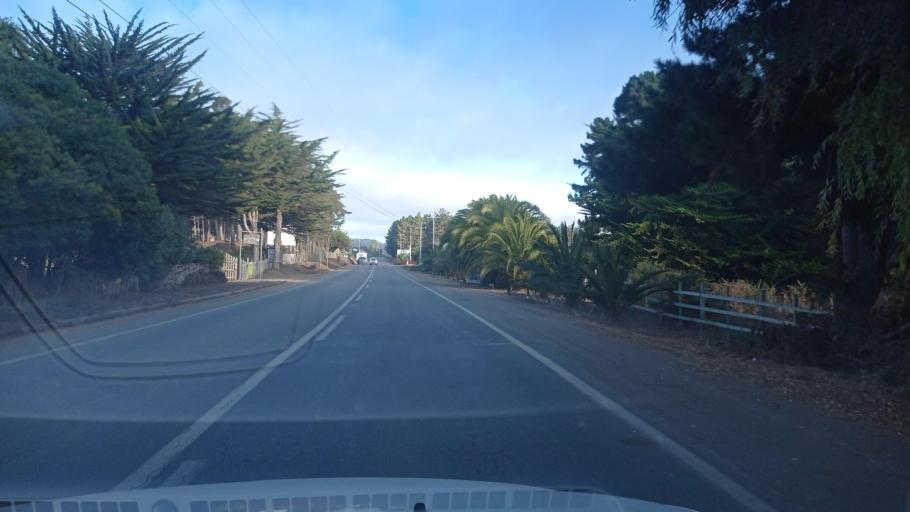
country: CL
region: O'Higgins
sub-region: Provincia de Colchagua
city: Santa Cruz
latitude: -34.4520
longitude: -72.0294
